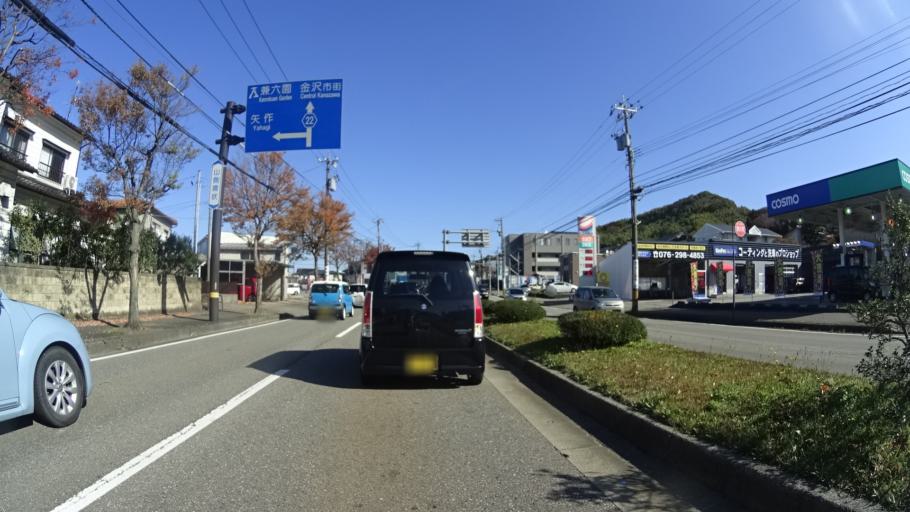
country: JP
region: Ishikawa
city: Nonoichi
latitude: 36.5173
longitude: 136.6331
